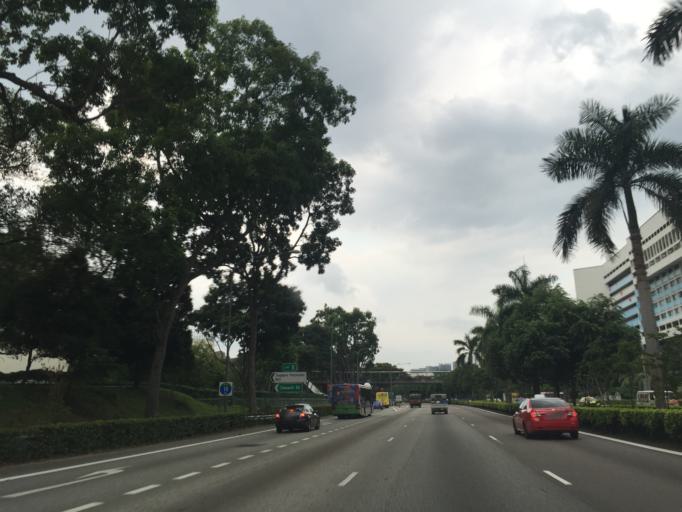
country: SG
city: Singapore
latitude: 1.3062
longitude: 103.7681
